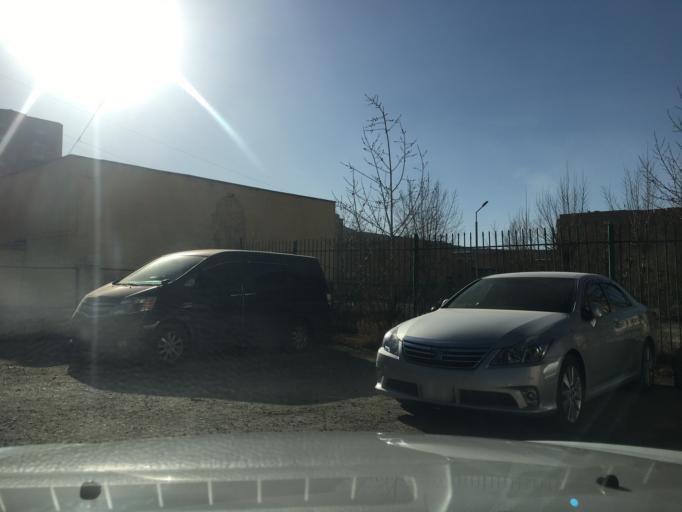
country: MN
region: Ulaanbaatar
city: Ulaanbaatar
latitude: 47.9148
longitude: 106.8512
